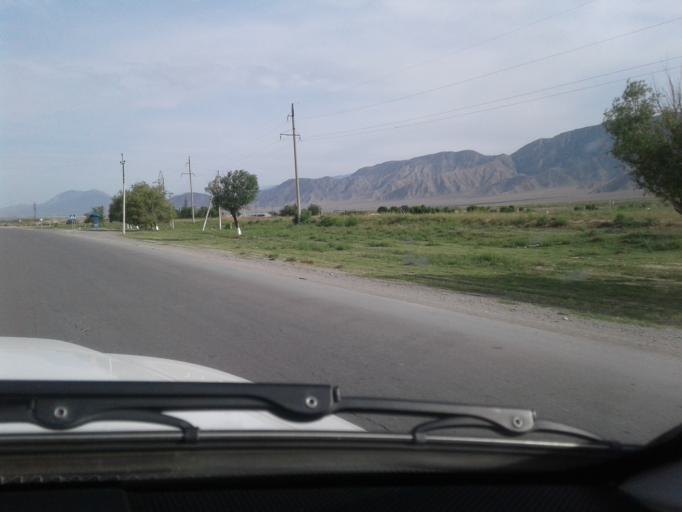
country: TM
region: Ahal
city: Arcabil
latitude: 38.1925
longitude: 57.8398
